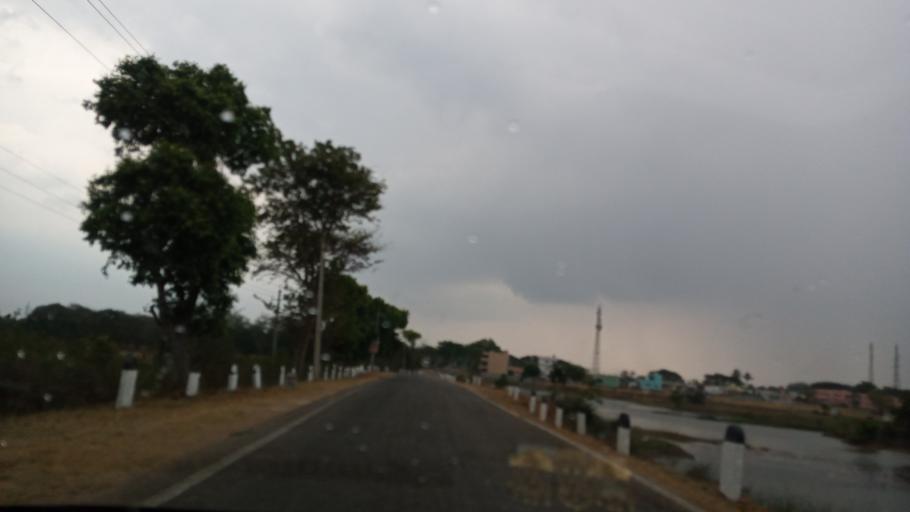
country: IN
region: Karnataka
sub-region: Kolar
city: Mulbagal
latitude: 13.1119
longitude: 78.3354
